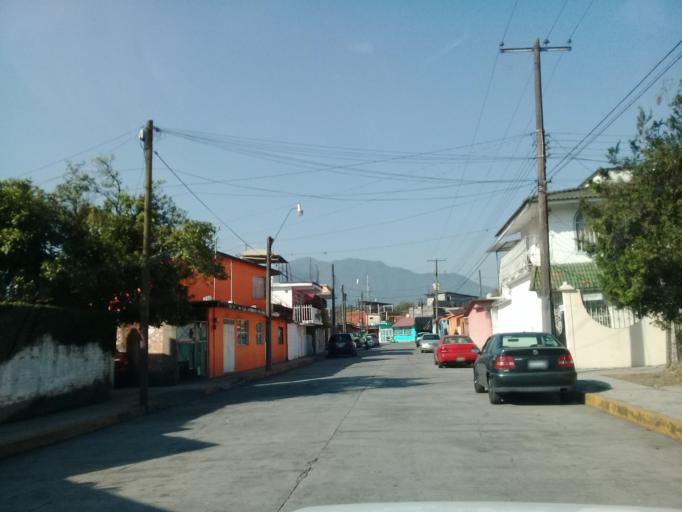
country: MX
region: Veracruz
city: Ixtac Zoquitlan
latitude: 18.8579
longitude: -97.0673
